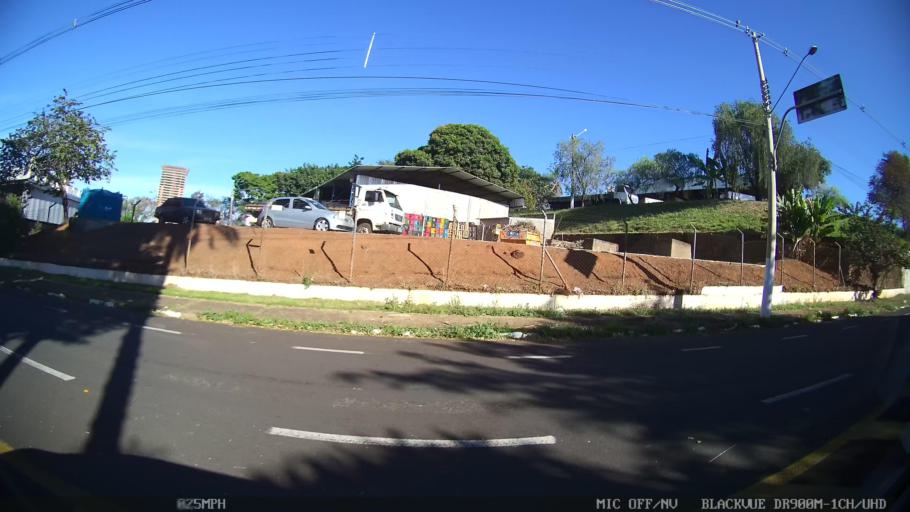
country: BR
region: Sao Paulo
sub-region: Franca
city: Franca
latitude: -20.5491
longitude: -47.4121
